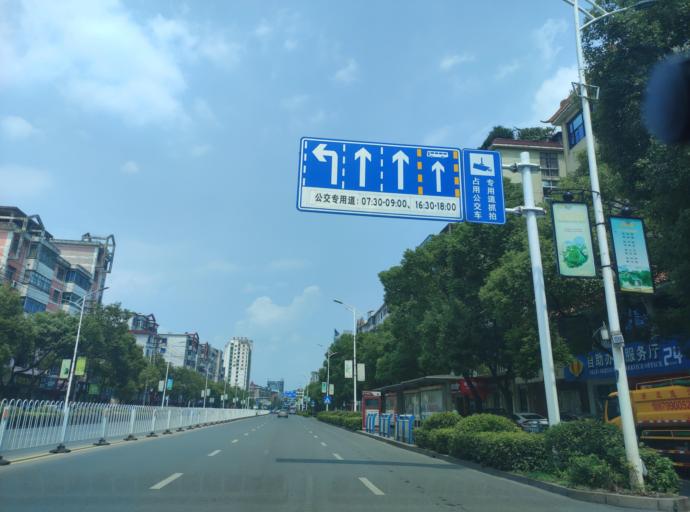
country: CN
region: Jiangxi Sheng
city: Pingxiang
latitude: 27.6389
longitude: 113.8604
